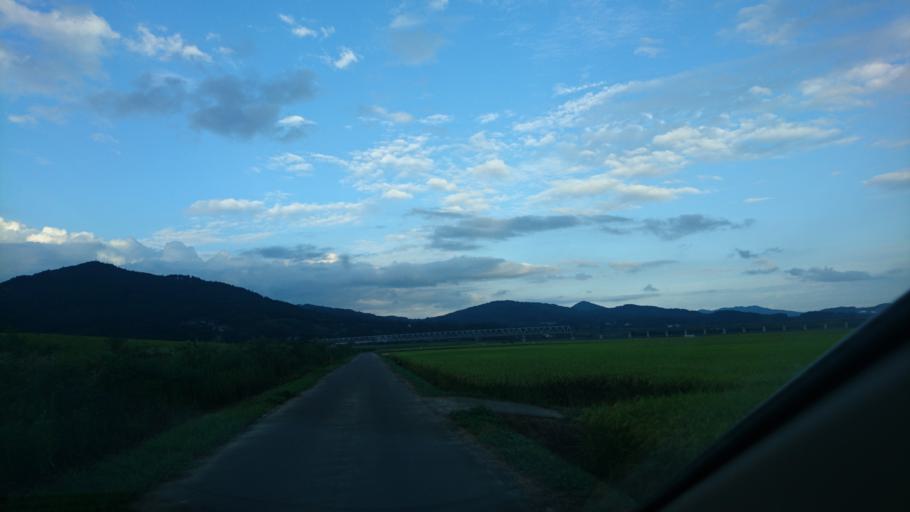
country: JP
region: Iwate
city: Ichinoseki
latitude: 38.9735
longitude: 141.1427
